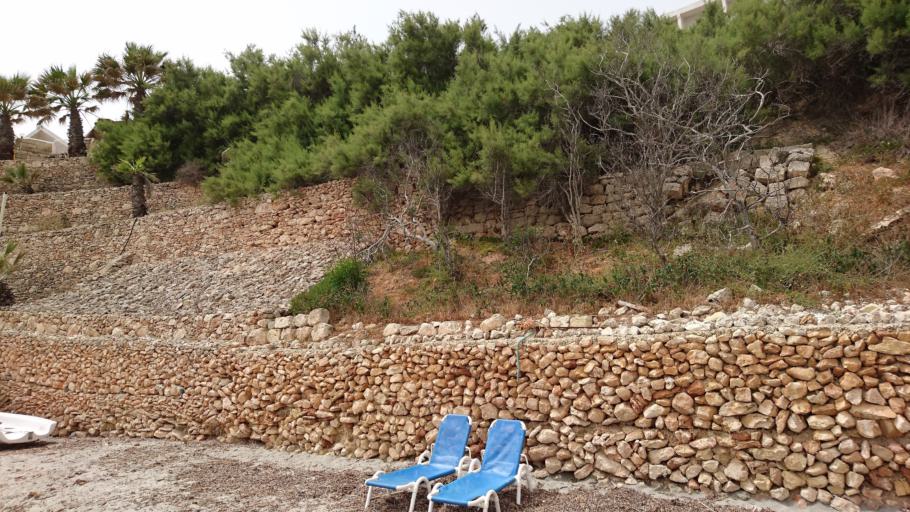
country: MT
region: Il-Mellieha
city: Mellieha
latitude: 35.9756
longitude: 14.3527
